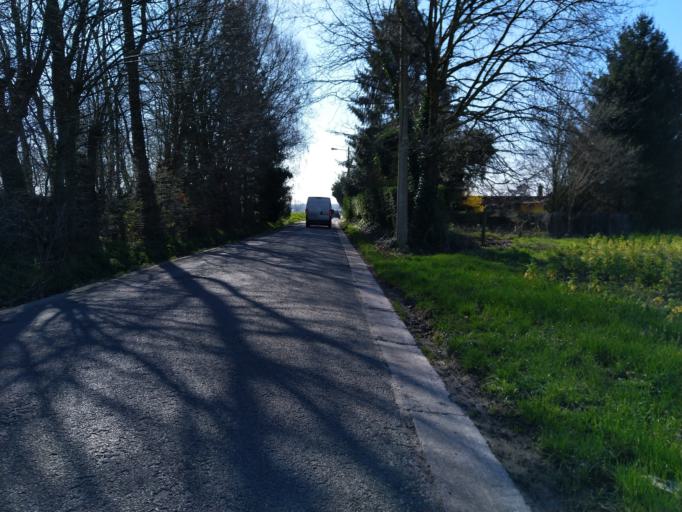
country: BE
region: Wallonia
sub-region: Province du Hainaut
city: Soignies
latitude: 50.5243
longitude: 4.0060
